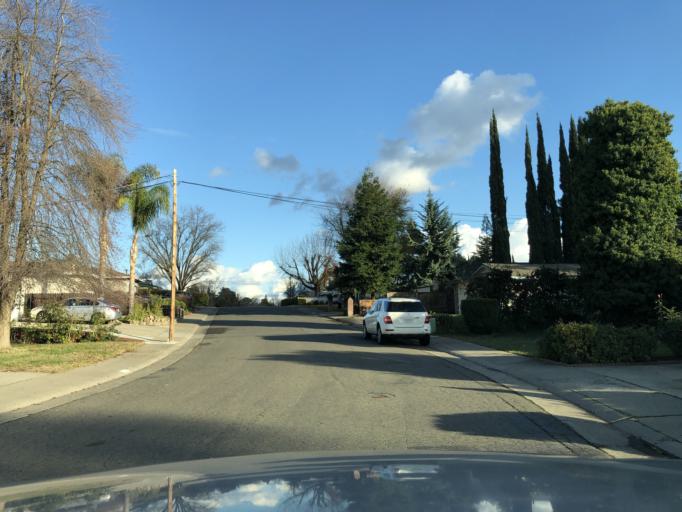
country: US
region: California
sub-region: Sacramento County
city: Foothill Farms
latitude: 38.6582
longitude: -121.3248
